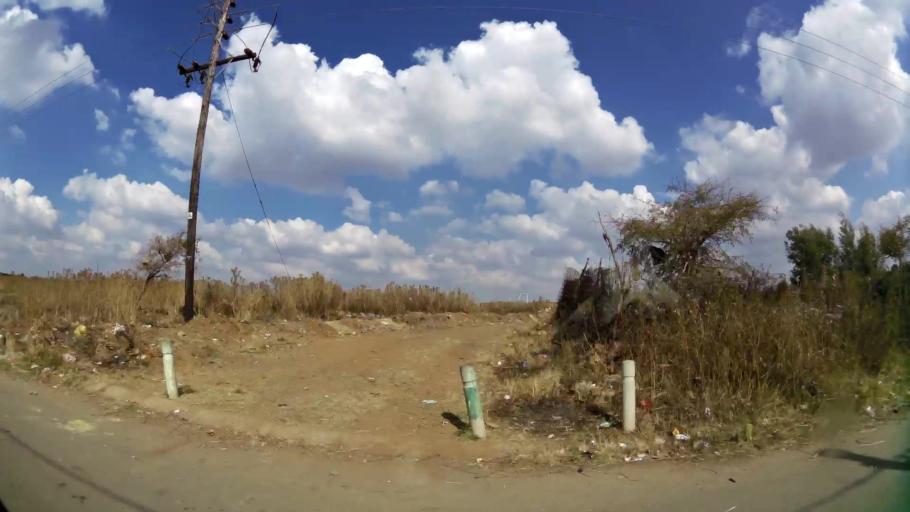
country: ZA
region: Gauteng
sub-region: City of Johannesburg Metropolitan Municipality
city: Roodepoort
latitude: -26.1849
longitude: 27.8419
